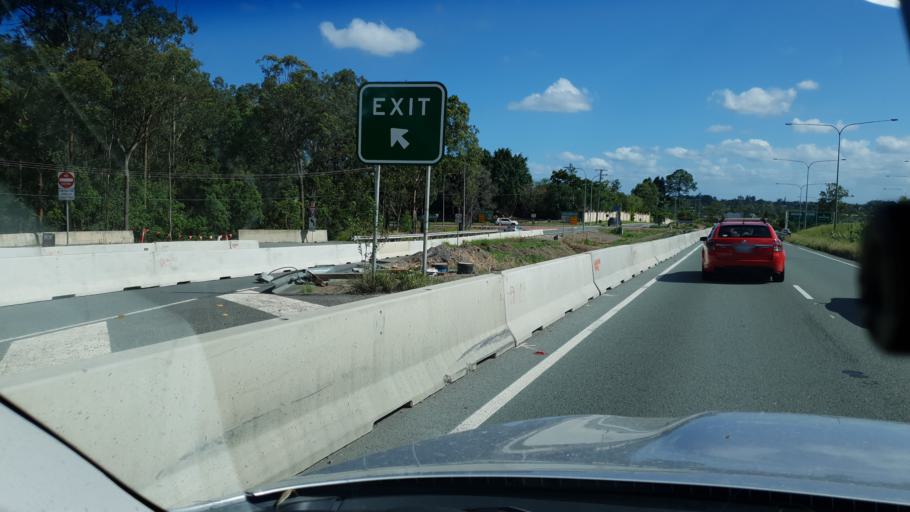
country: AU
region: Queensland
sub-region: Brisbane
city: Sunnybank Hills
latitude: -27.6527
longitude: 153.0407
